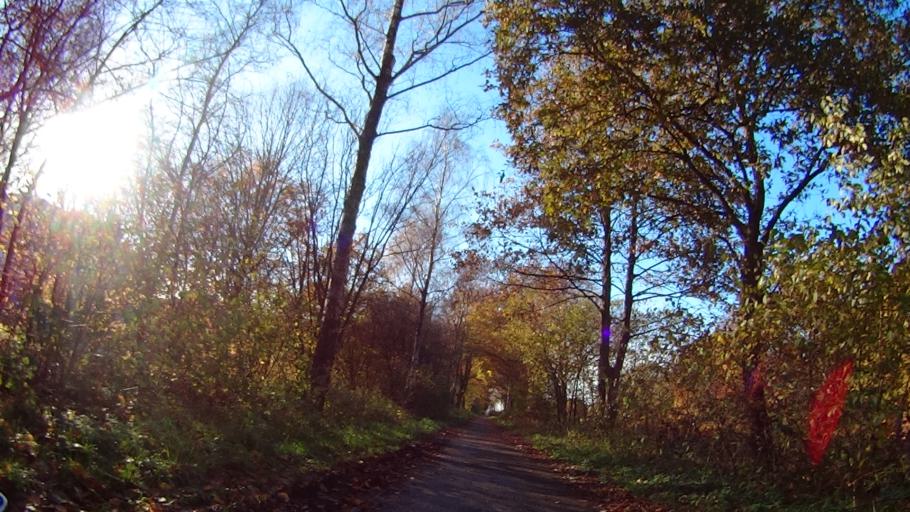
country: NL
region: Utrecht
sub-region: Gemeente Zeist
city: Zeist
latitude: 52.1415
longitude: 5.2474
